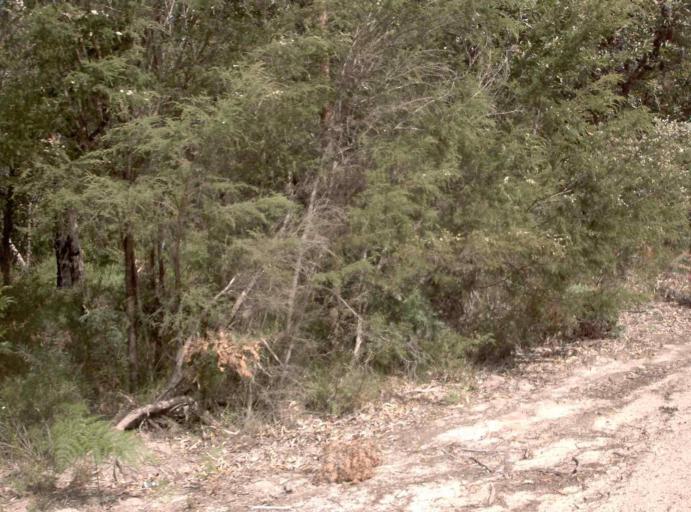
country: AU
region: New South Wales
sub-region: Bega Valley
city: Eden
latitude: -37.4917
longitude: 149.6627
